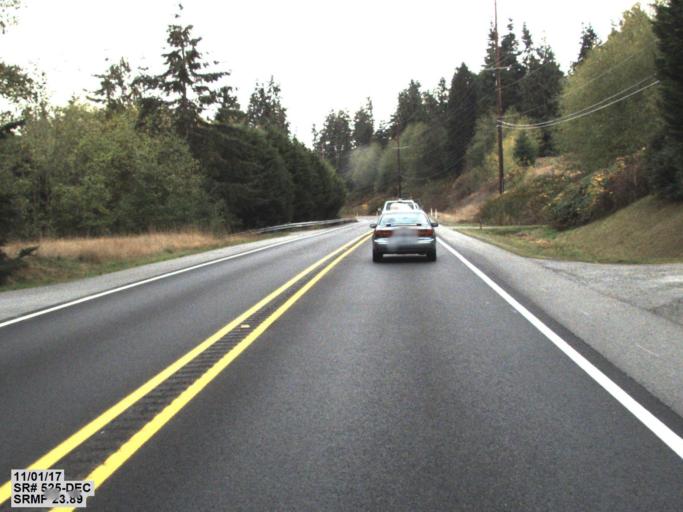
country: US
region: Washington
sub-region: Island County
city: Freeland
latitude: 48.0815
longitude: -122.5703
